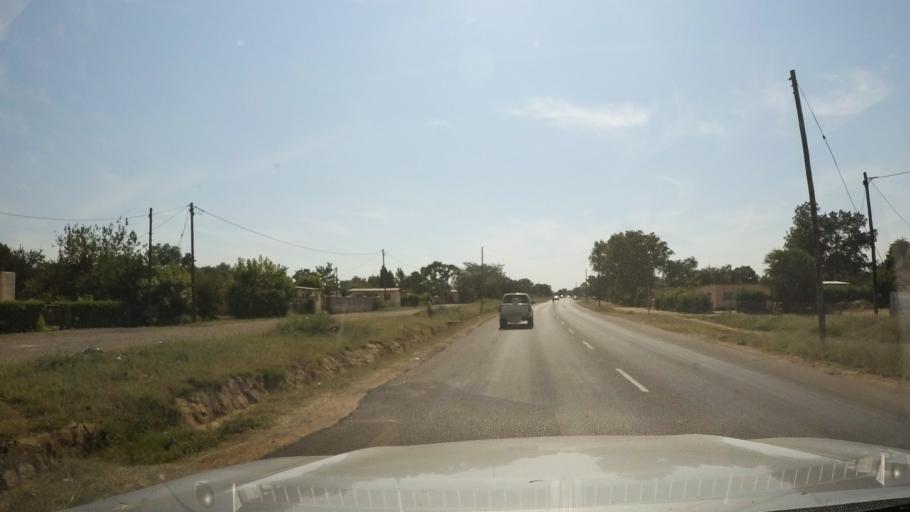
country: BW
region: South East
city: Lobatse
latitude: -25.2096
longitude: 25.6830
